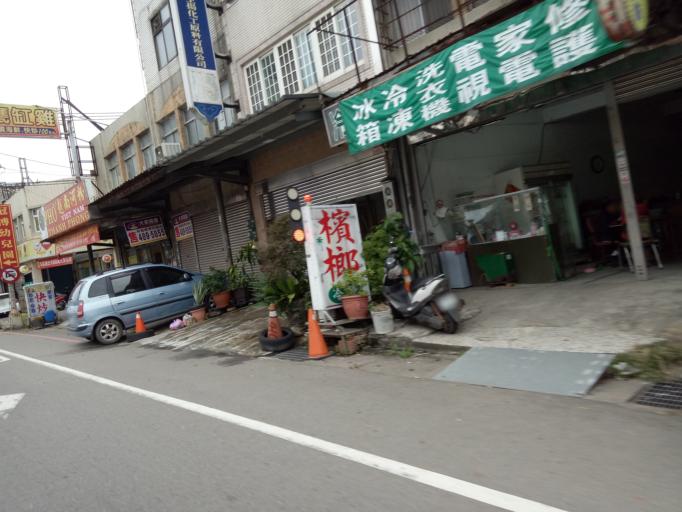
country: TW
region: Taiwan
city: Daxi
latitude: 24.8727
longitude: 121.2290
